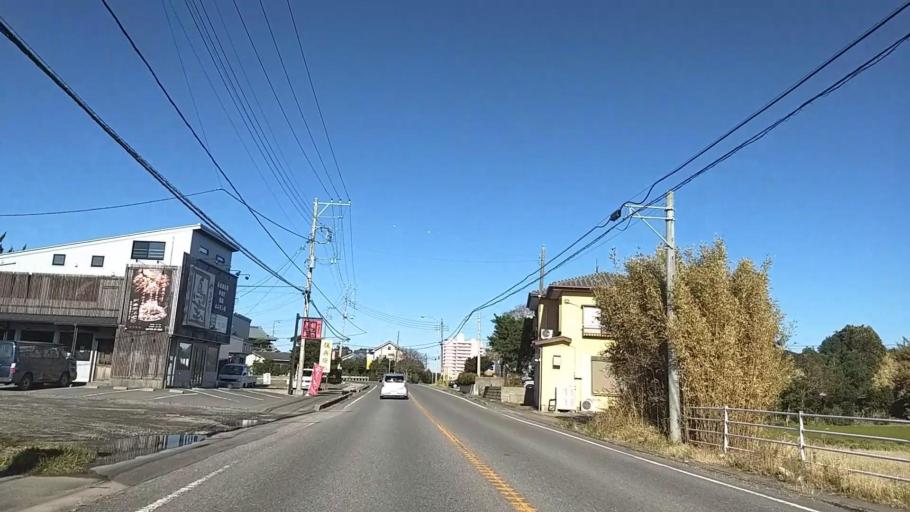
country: JP
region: Chiba
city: Ohara
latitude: 35.3176
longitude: 140.4029
